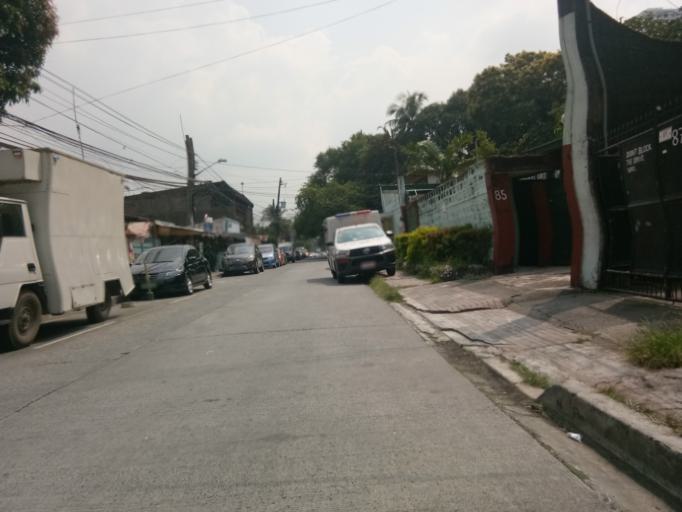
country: PH
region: Metro Manila
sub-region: San Juan
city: San Juan
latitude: 14.6164
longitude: 121.0549
